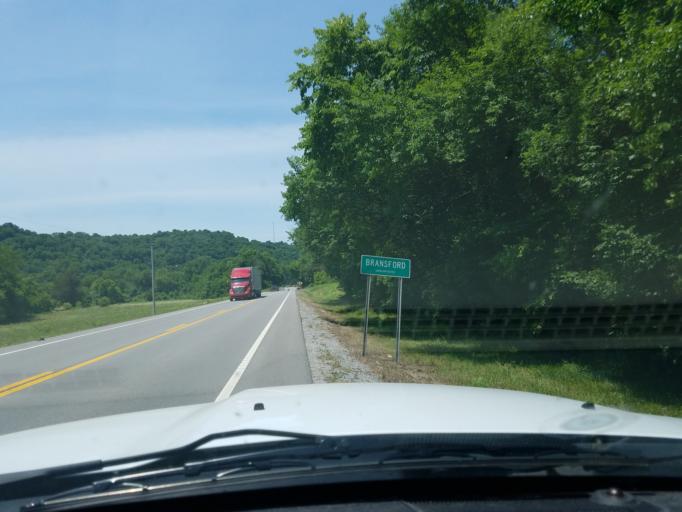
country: US
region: Tennessee
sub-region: Sumner County
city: Westmoreland
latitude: 36.4962
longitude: -86.2759
